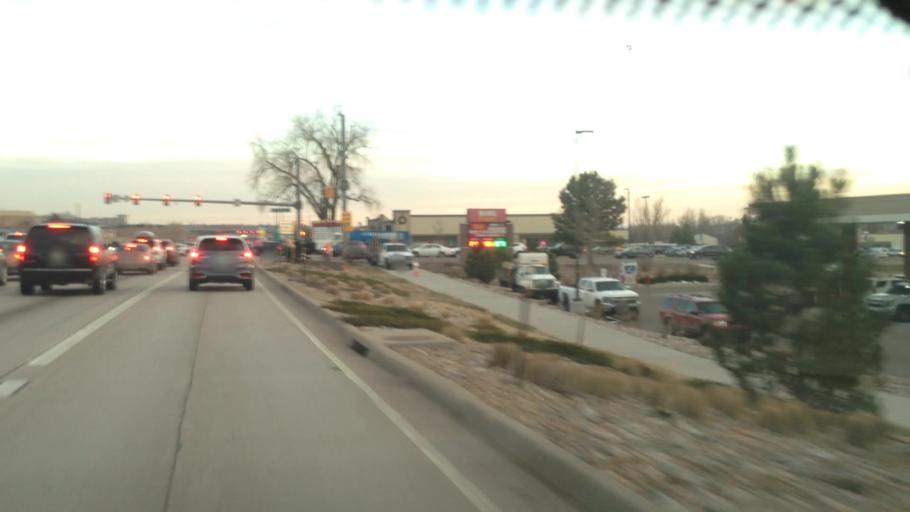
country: US
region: Colorado
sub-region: Douglas County
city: Stonegate
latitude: 39.5593
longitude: -104.7808
